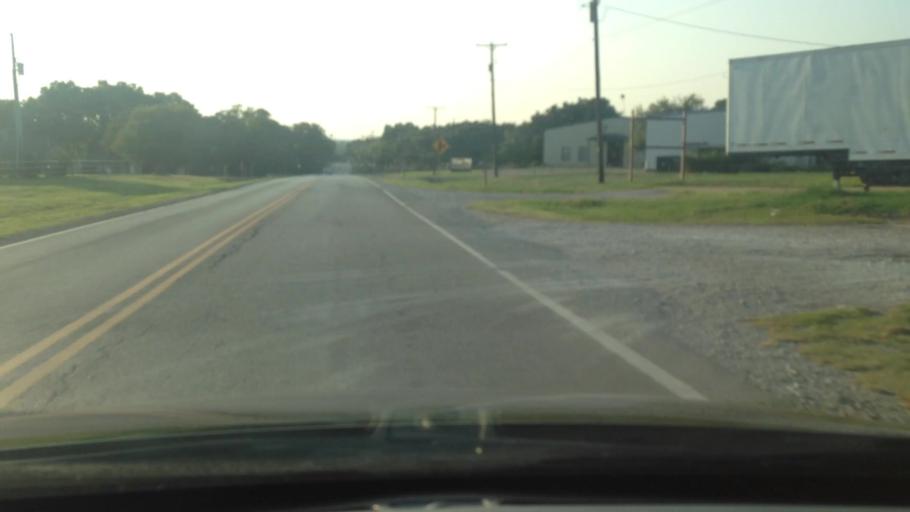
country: US
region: Texas
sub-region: Tarrant County
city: Rendon
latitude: 32.5939
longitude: -97.2555
